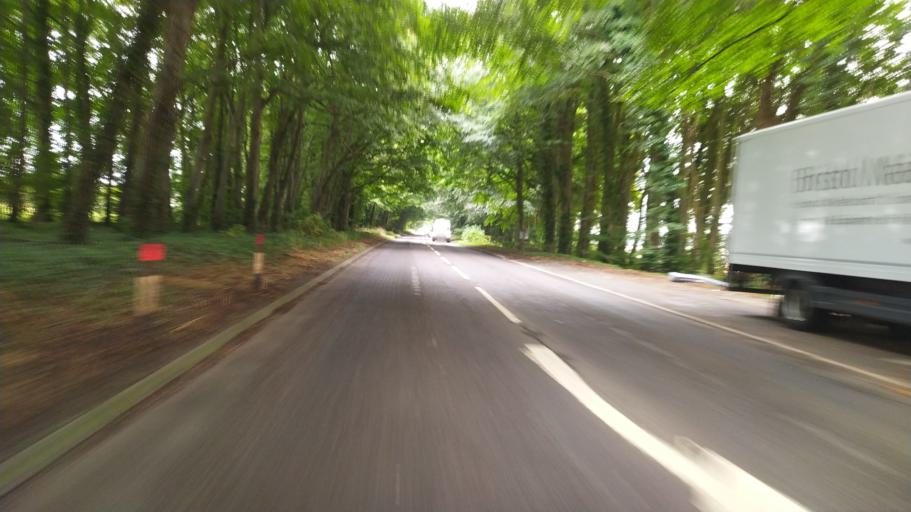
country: GB
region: England
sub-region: Wiltshire
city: Salisbury
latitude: 51.0461
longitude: -1.8314
